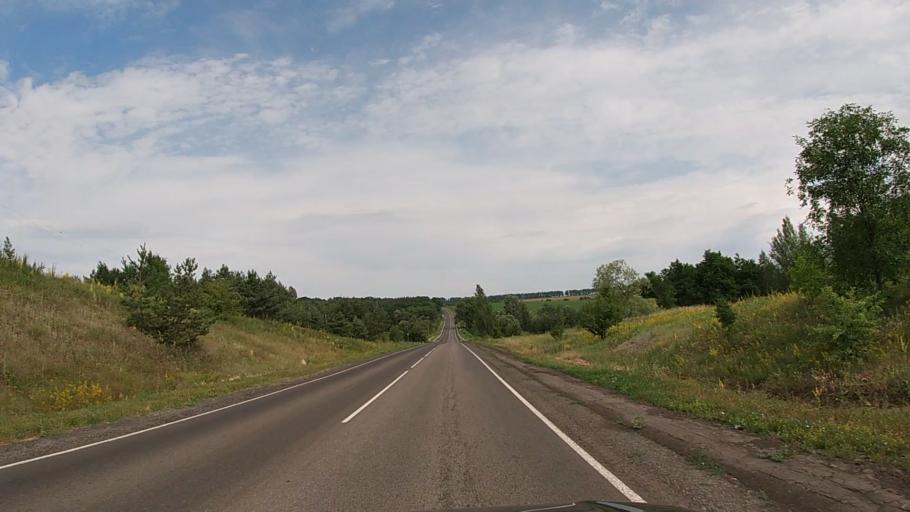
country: RU
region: Belgorod
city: Krasnaya Yaruga
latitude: 50.8253
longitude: 35.4988
